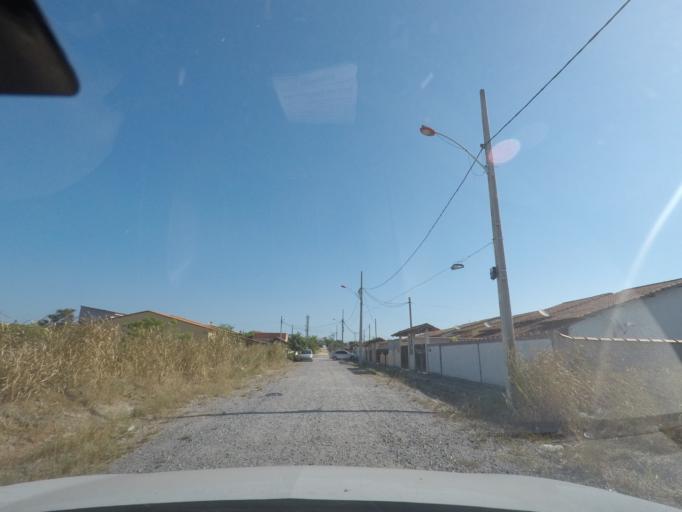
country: BR
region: Rio de Janeiro
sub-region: Marica
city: Marica
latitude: -22.9657
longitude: -42.9155
